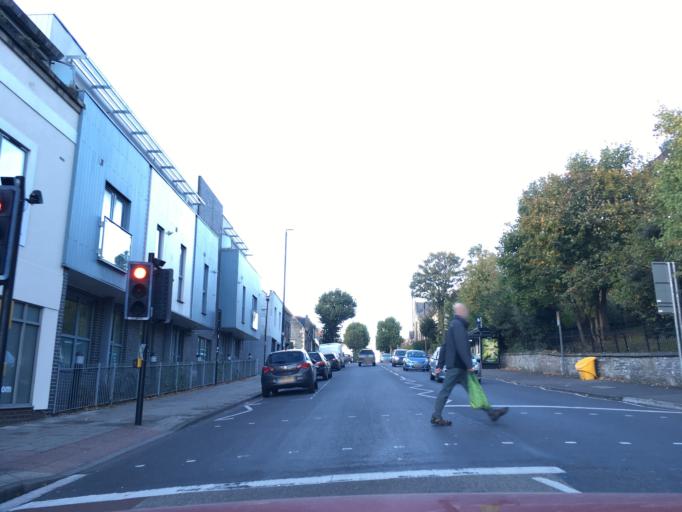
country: GB
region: England
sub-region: Bristol
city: Bristol
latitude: 51.4769
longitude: -2.5904
